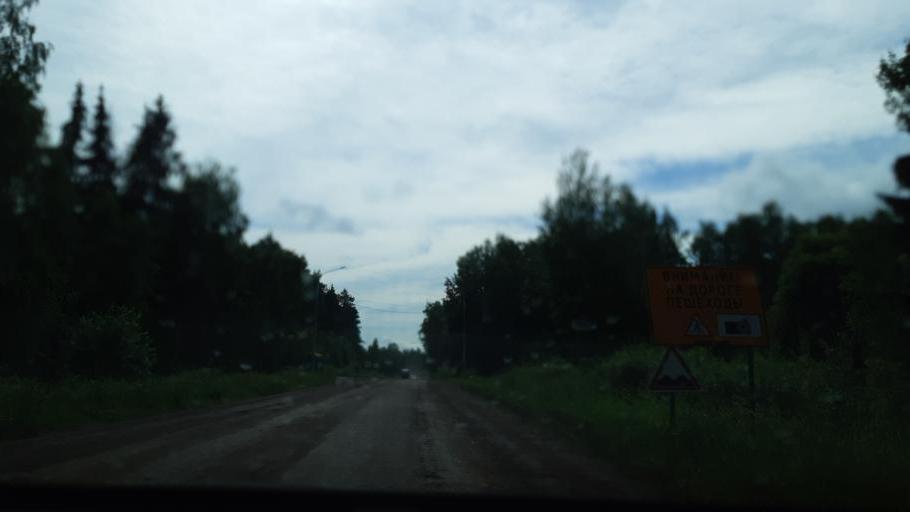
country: RU
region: Moskovskaya
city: Vereya
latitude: 55.3133
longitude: 36.1223
